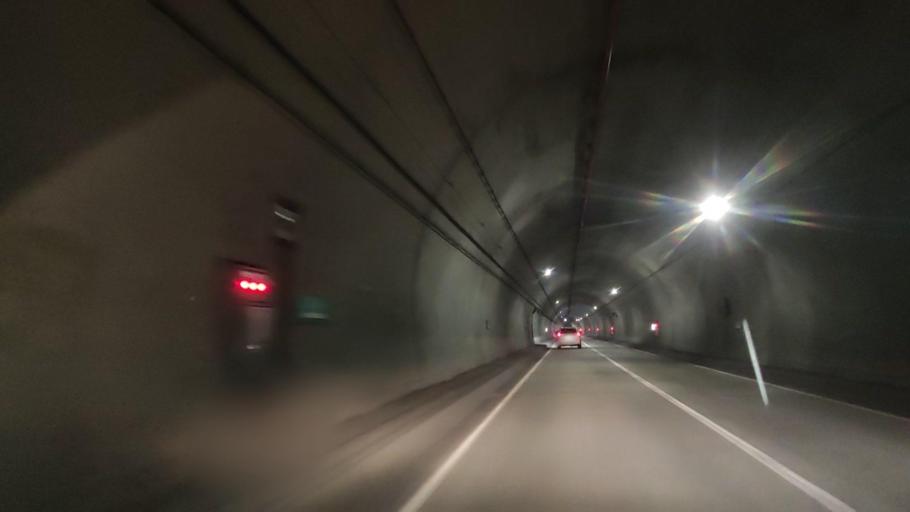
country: JP
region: Hokkaido
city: Rumoi
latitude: 43.7141
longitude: 141.3304
